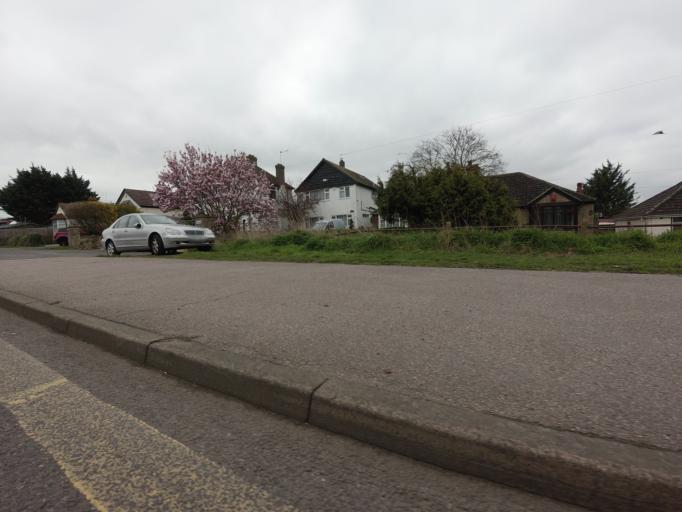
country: GB
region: England
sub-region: Greater London
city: Bexley
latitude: 51.4113
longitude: 0.1407
